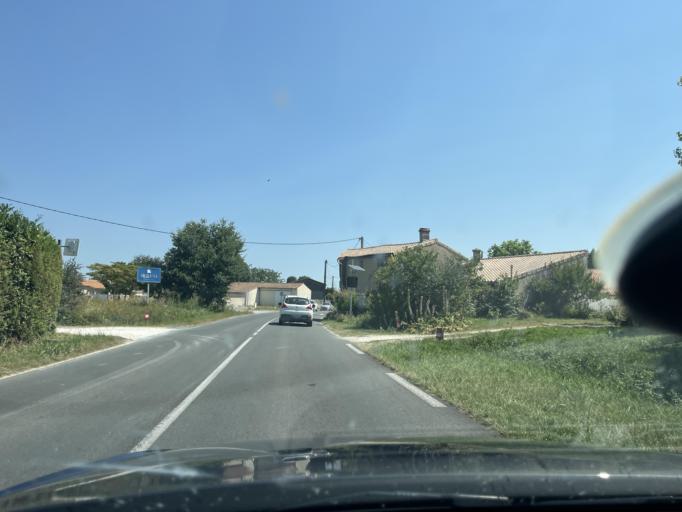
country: FR
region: Poitou-Charentes
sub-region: Departement de la Charente-Maritime
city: Cozes
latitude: 45.5465
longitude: -0.7868
